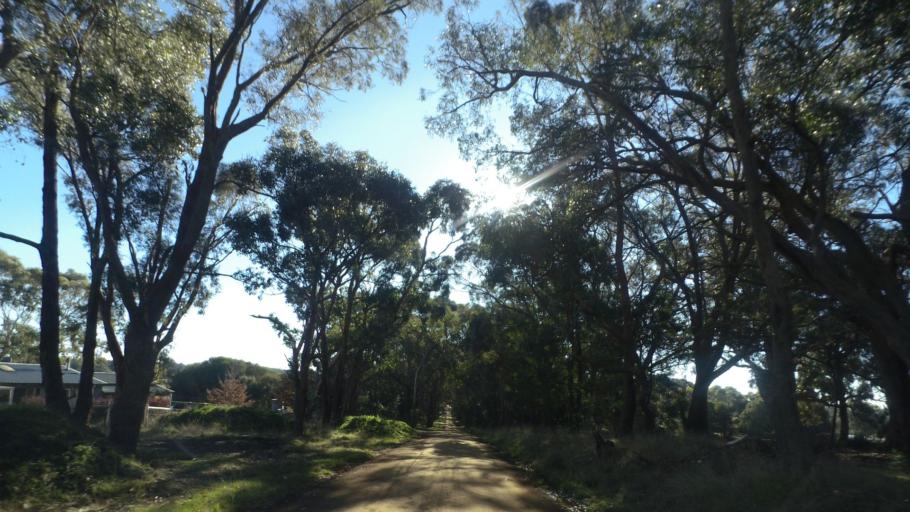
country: AU
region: Victoria
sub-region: Mount Alexander
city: Castlemaine
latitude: -37.2973
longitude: 144.3334
